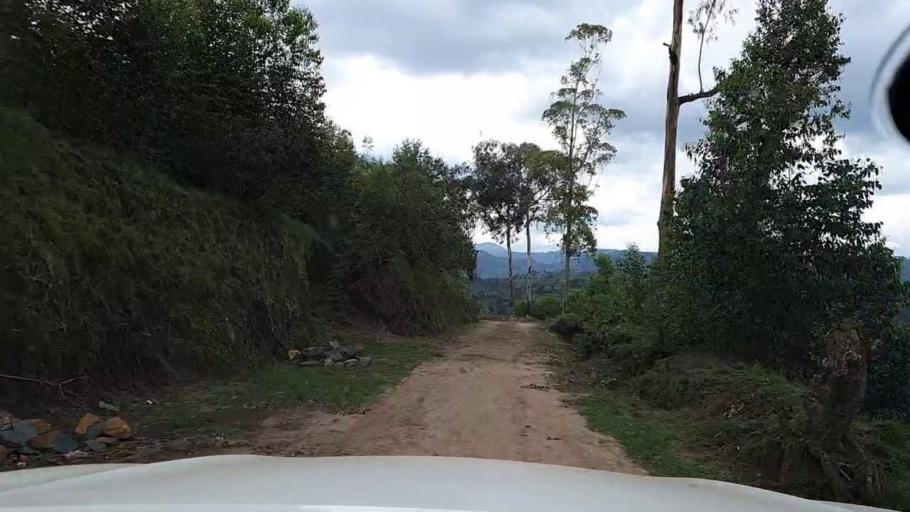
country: RW
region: Southern Province
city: Nzega
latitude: -2.6387
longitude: 29.4801
